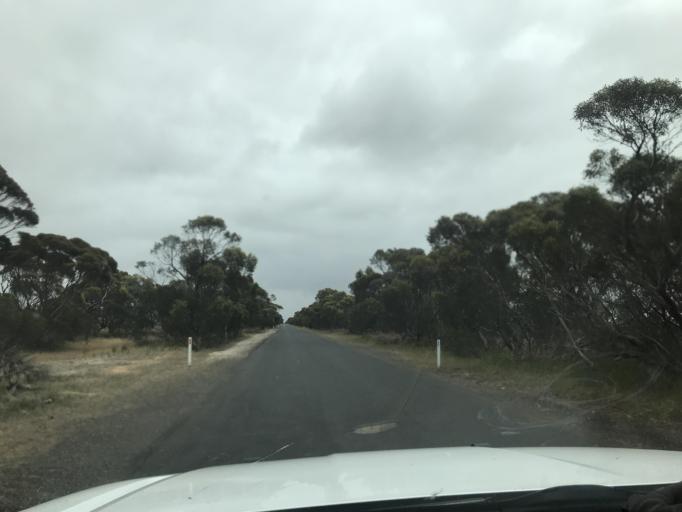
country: AU
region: South Australia
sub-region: Tatiara
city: Bordertown
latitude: -36.1207
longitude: 141.0653
